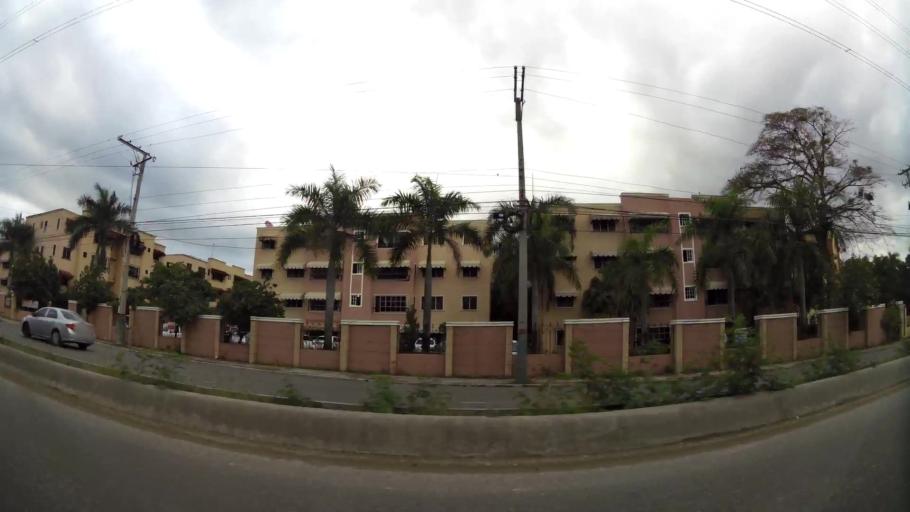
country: DO
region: Nacional
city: Santo Domingo
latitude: 18.5067
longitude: -69.9756
